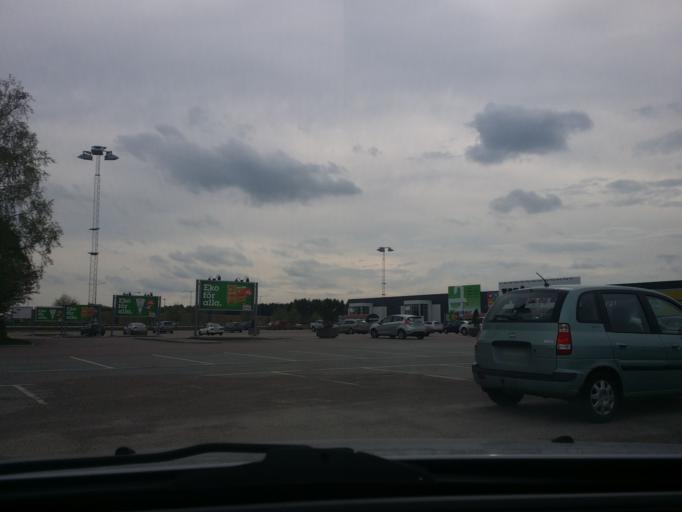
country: SE
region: Vaestmanland
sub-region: Vasteras
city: Vasteras
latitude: 59.6085
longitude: 16.6217
